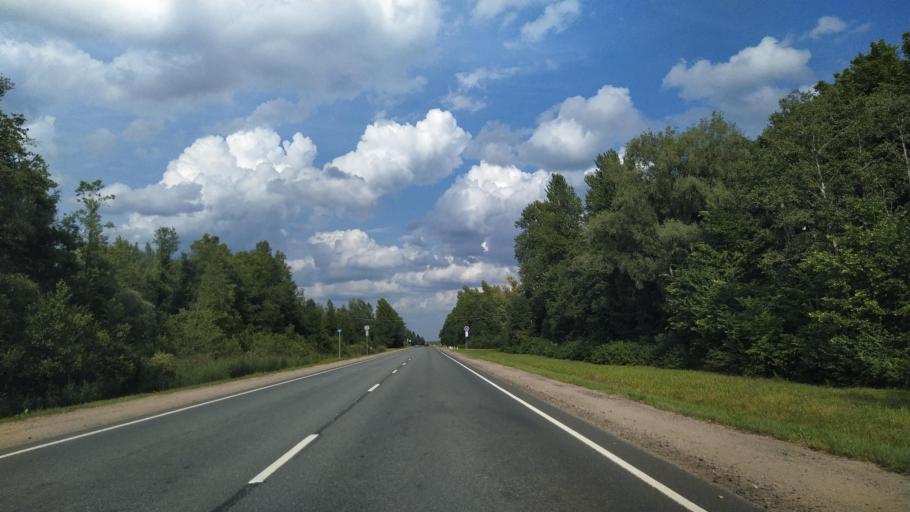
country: RU
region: Novgorod
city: Shimsk
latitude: 58.1868
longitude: 30.5544
